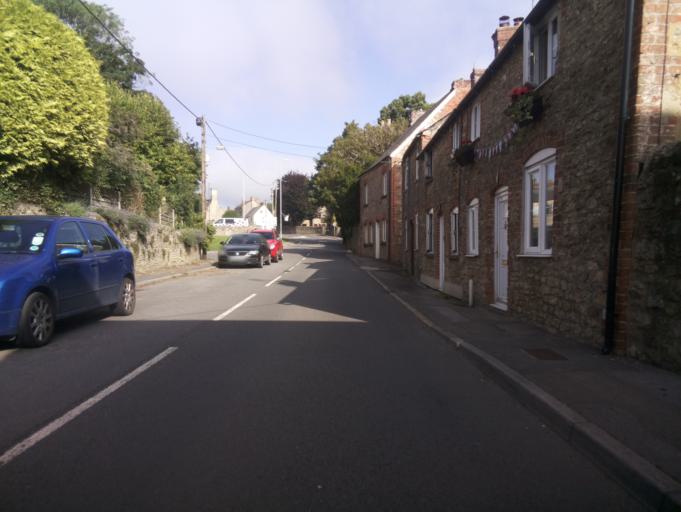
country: GB
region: England
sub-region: Borough of Swindon
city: Highworth
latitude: 51.6301
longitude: -1.7067
